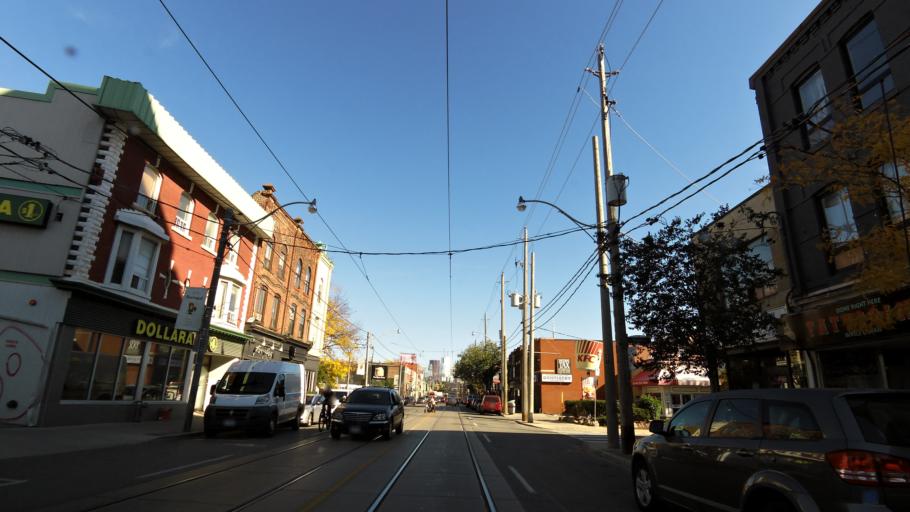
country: CA
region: Ontario
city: Toronto
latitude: 43.6494
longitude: -79.4236
